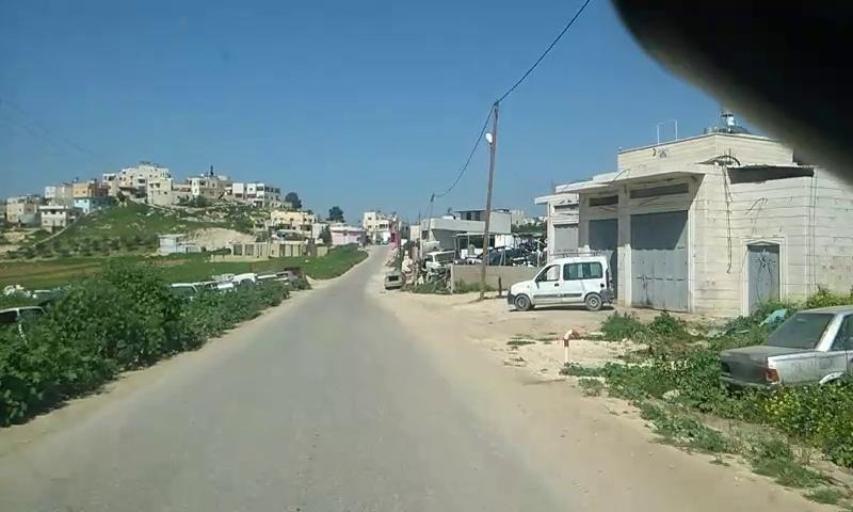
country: PS
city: Dayr Samit
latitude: 31.5158
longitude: 34.9709
